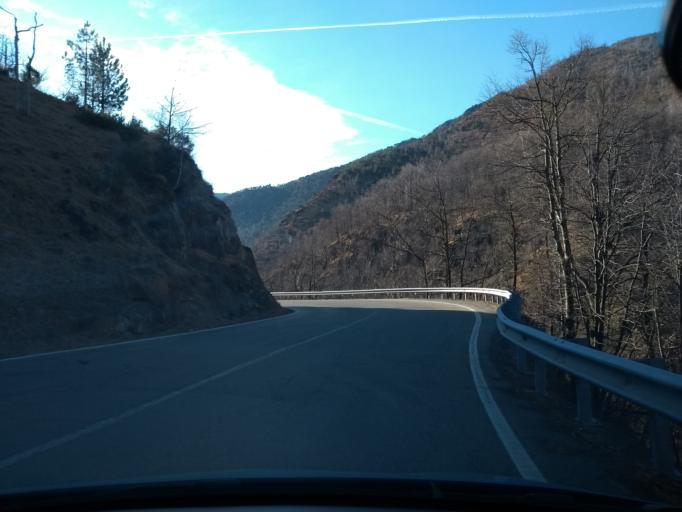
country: IT
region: Piedmont
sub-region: Provincia di Torino
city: La Villa
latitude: 45.2554
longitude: 7.4363
